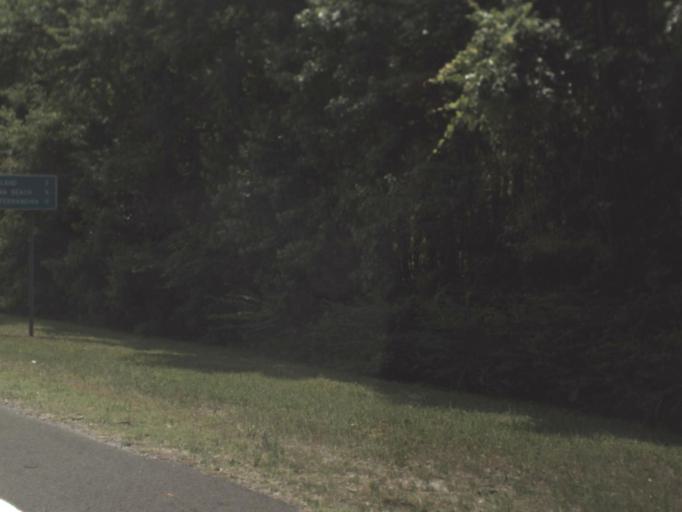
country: US
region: Florida
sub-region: Nassau County
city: Yulee
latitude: 30.6315
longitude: -81.5957
